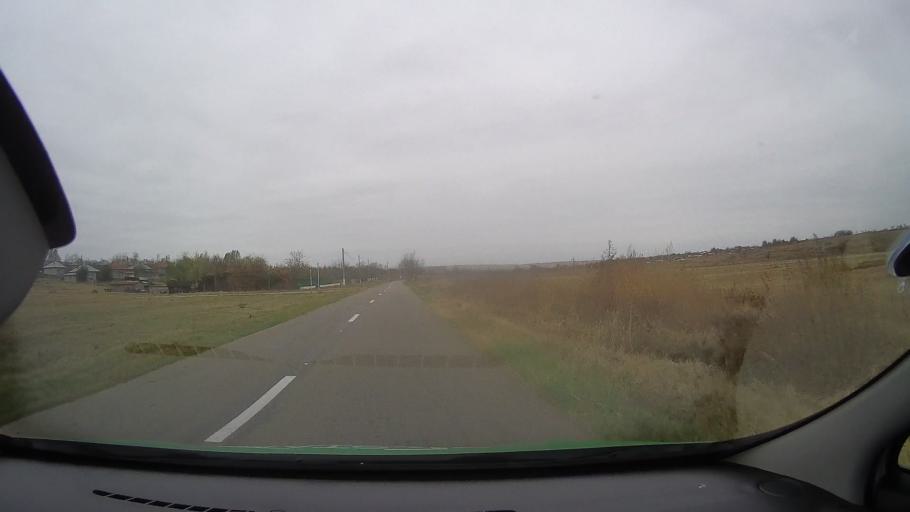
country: RO
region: Constanta
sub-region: Comuna Saraiu
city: Saraiu
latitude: 44.7243
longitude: 28.1690
